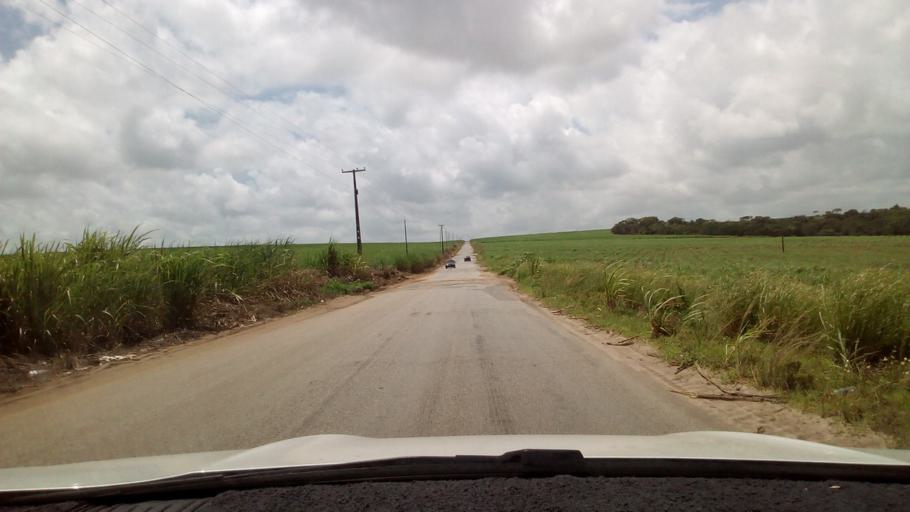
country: BR
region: Paraiba
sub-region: Caapora
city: Caapora
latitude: -7.4862
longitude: -34.9188
